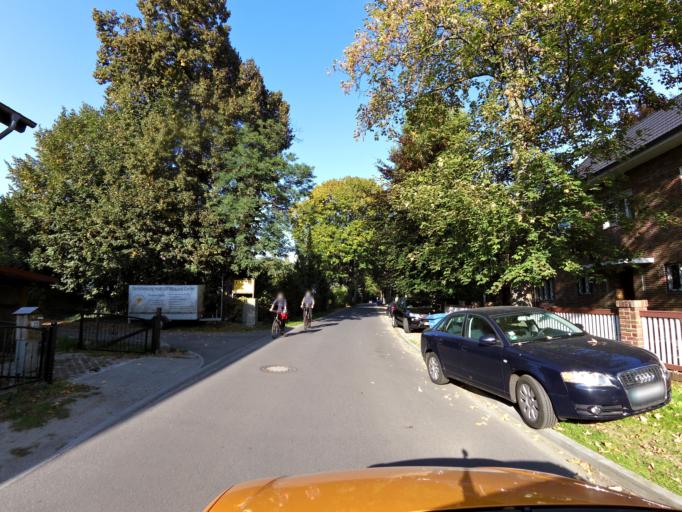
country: DE
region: Brandenburg
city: Potsdam
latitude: 52.4312
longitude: 13.0997
